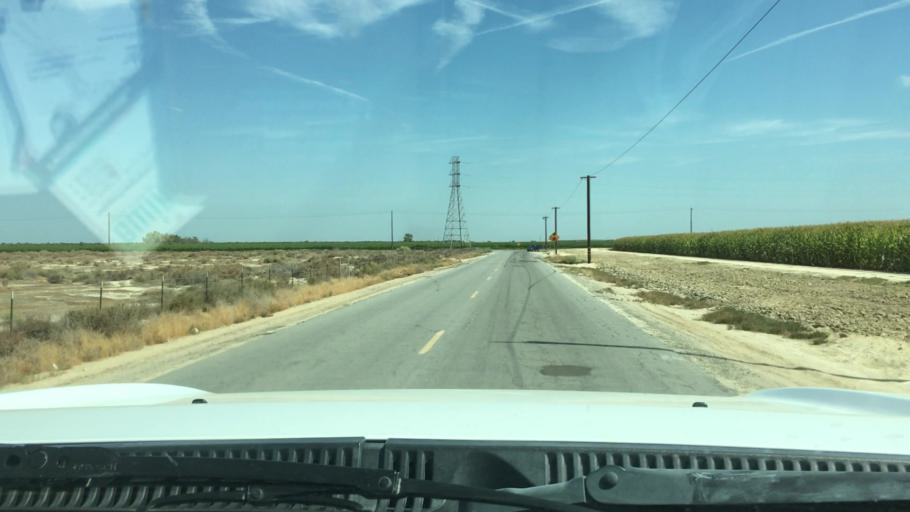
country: US
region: California
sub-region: Kern County
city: Buttonwillow
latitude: 35.4399
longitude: -119.3759
